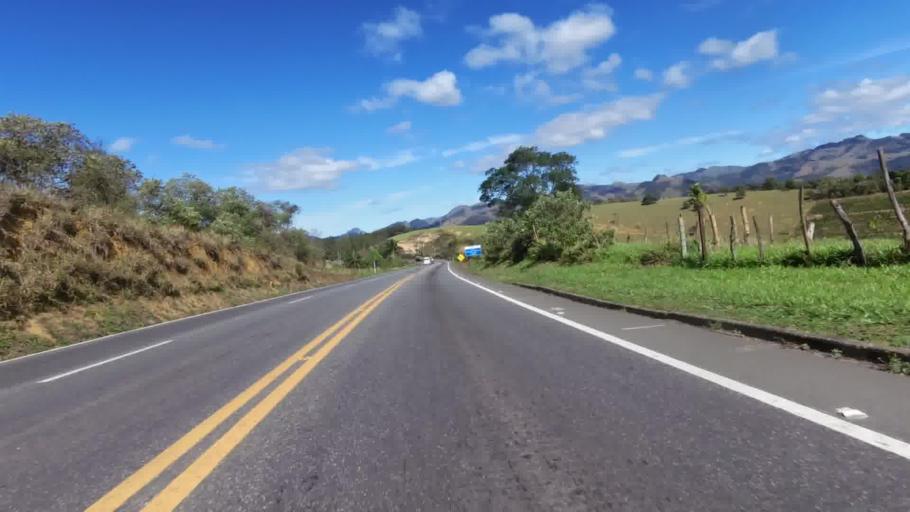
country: BR
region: Espirito Santo
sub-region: Alfredo Chaves
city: Alfredo Chaves
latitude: -20.6977
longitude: -40.7118
